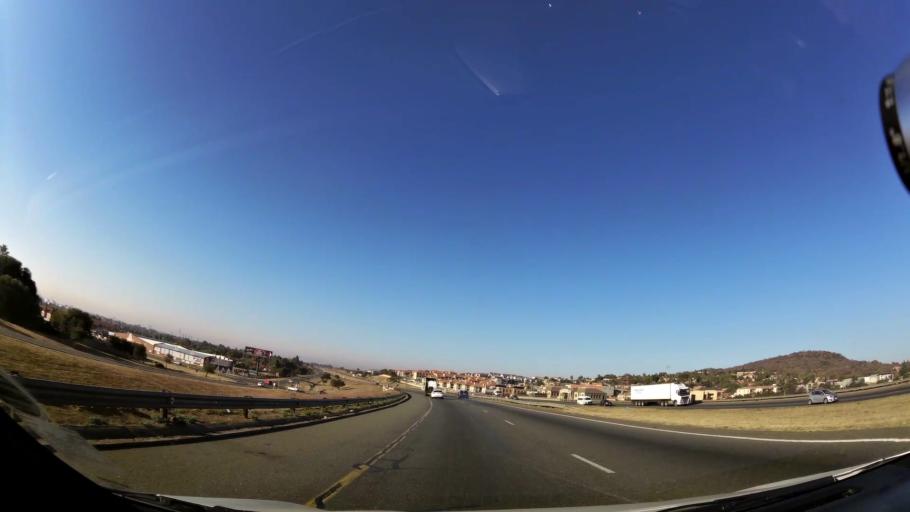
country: ZA
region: Gauteng
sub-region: Ekurhuleni Metropolitan Municipality
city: Germiston
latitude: -26.2856
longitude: 28.1015
